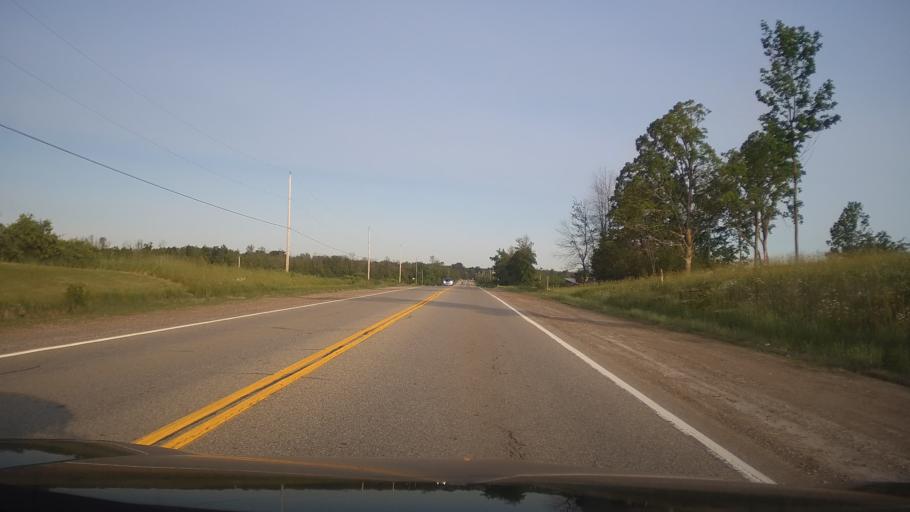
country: CA
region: Ontario
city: Carleton Place
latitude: 45.1240
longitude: -76.1465
